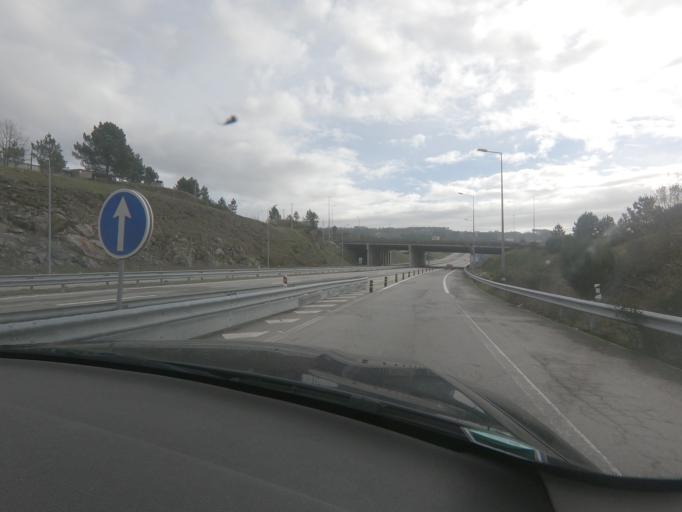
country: PT
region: Vila Real
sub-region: Vila Real
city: Vila Real
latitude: 41.3254
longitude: -7.6986
